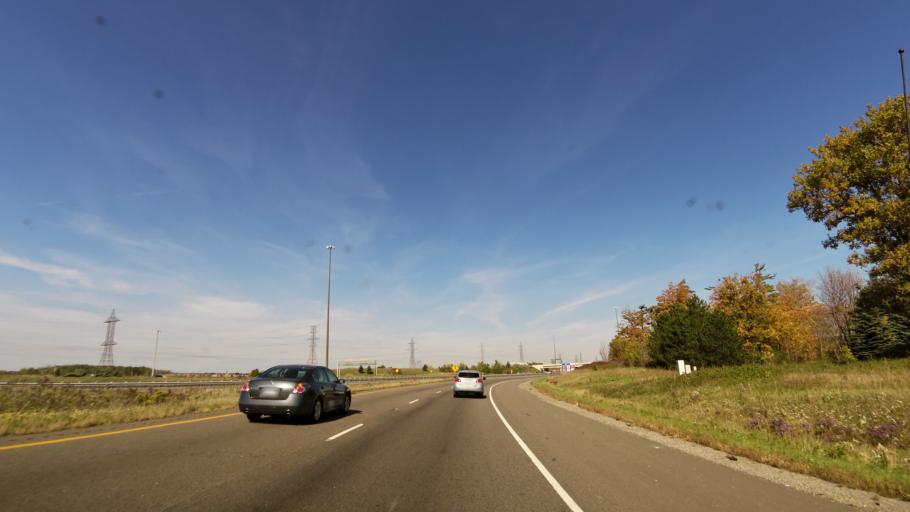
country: CA
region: Ontario
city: Mississauga
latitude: 43.5302
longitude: -79.7223
